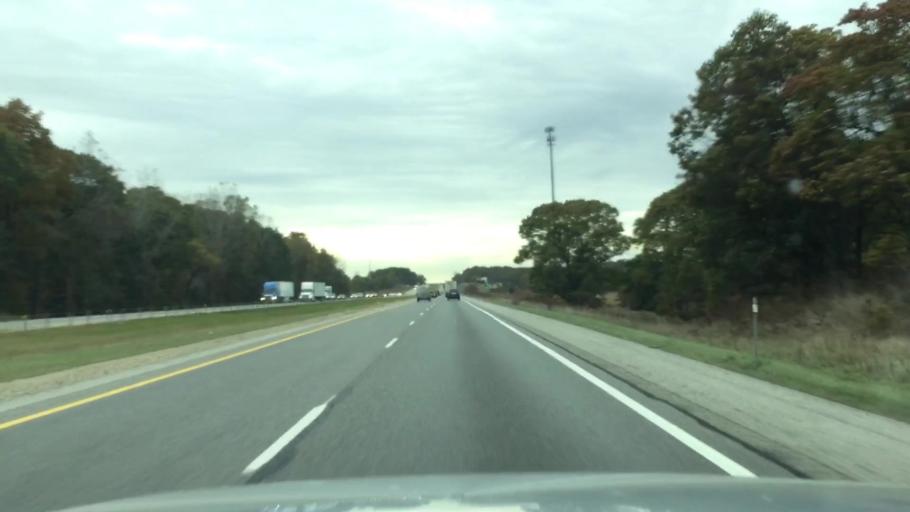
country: US
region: Michigan
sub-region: Van Buren County
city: Mattawan
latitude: 42.2233
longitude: -85.7488
